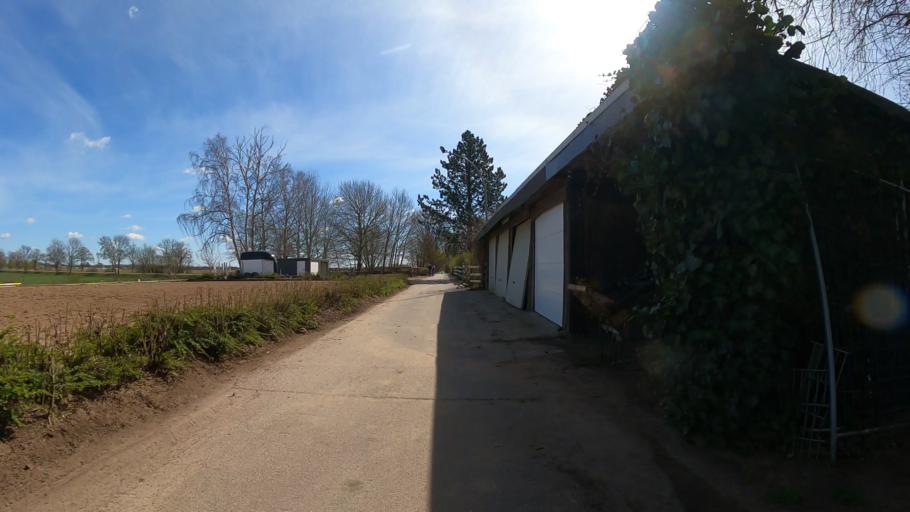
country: DE
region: Lower Saxony
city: Stelle
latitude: 53.4599
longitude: 10.1089
